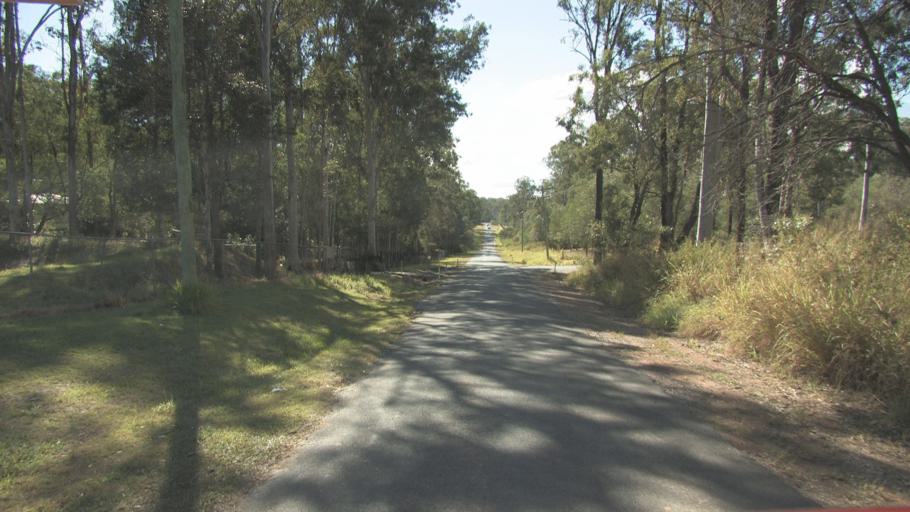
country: AU
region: Queensland
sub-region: Logan
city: Chambers Flat
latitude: -27.8098
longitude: 153.0820
